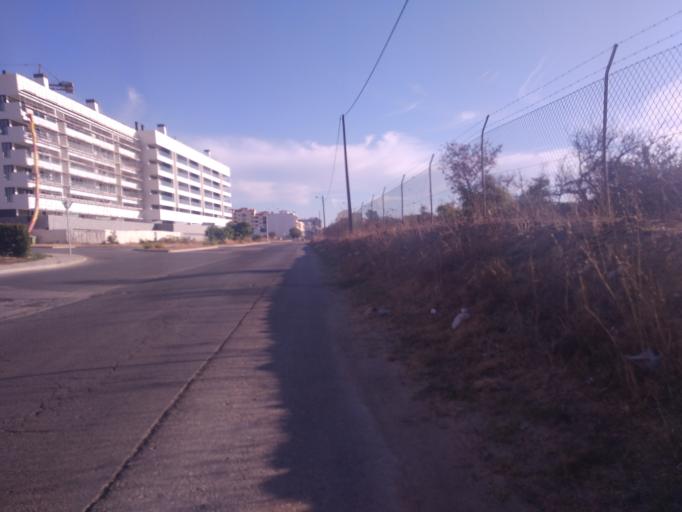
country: PT
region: Faro
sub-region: Faro
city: Faro
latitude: 37.0313
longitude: -7.9399
